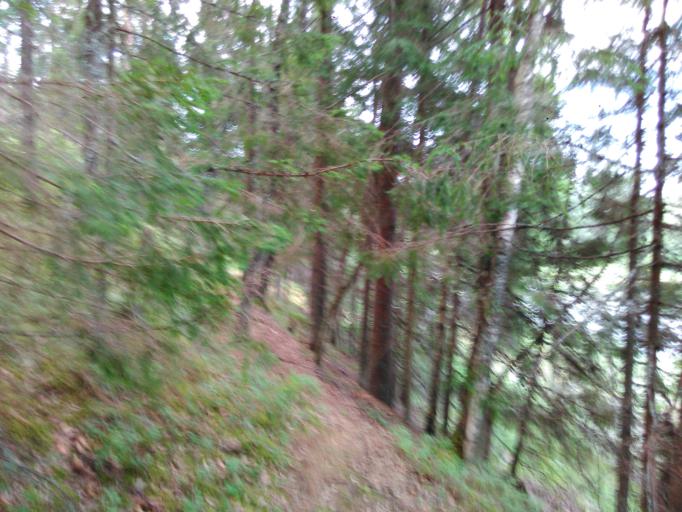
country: RU
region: Tverskaya
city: Ostashkov
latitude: 57.2441
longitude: 33.0120
